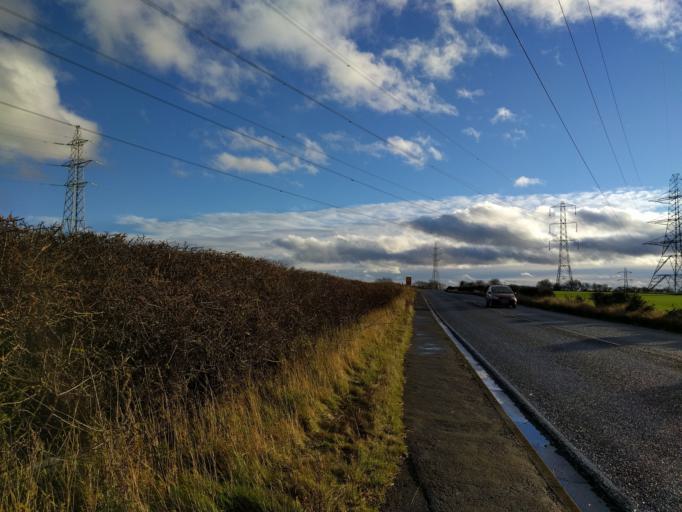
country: GB
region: England
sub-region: Northumberland
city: Bedlington
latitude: 55.1160
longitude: -1.5739
